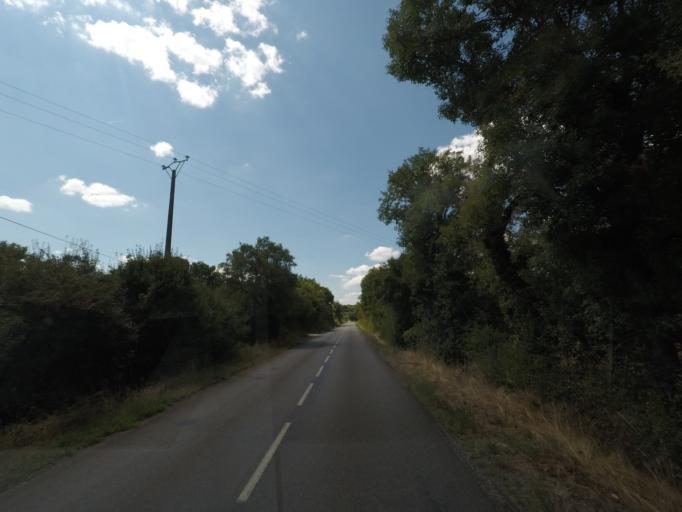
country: FR
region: Midi-Pyrenees
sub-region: Departement du Lot
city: Lacapelle-Marival
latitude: 44.6244
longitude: 1.8645
